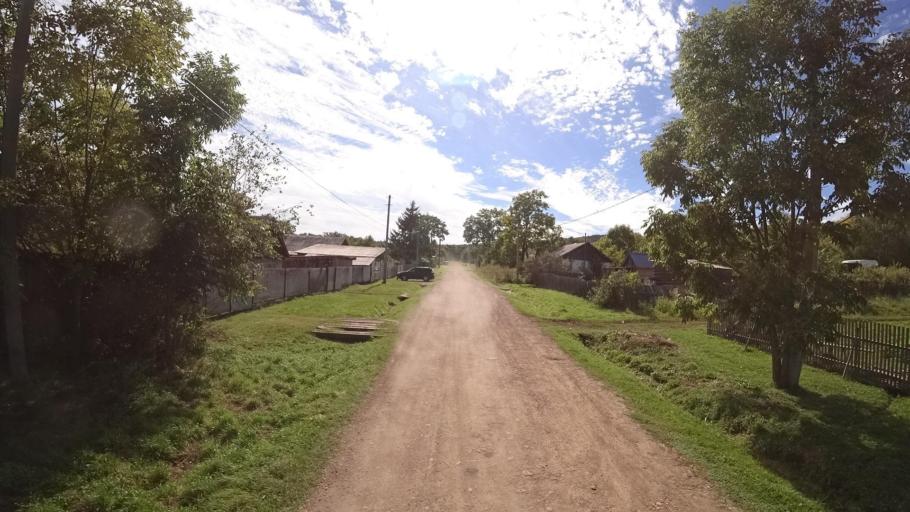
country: RU
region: Primorskiy
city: Yakovlevka
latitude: 44.3961
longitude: 133.5989
